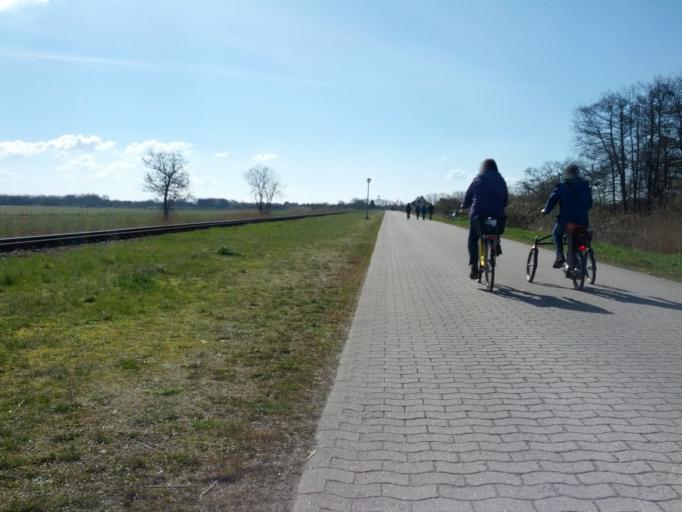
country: DE
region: Lower Saxony
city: Langeoog
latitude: 53.7374
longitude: 7.4913
